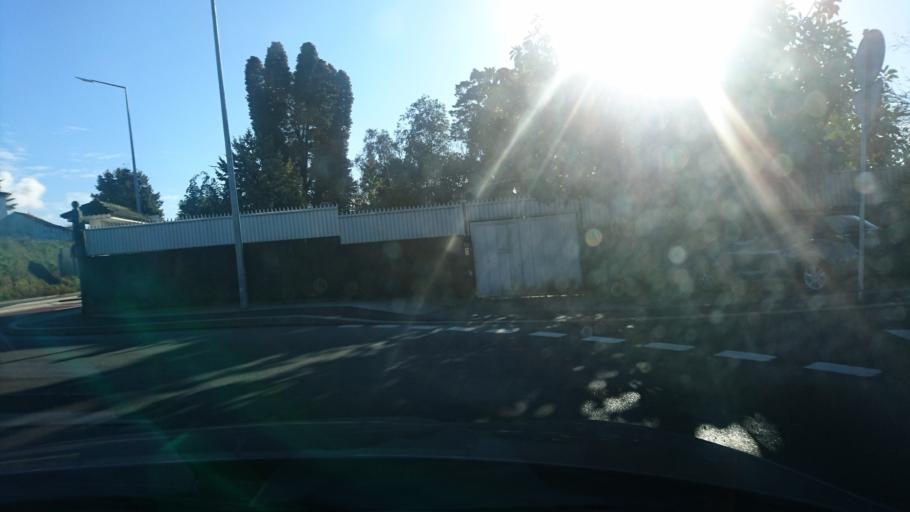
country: PT
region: Aveiro
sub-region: Santa Maria da Feira
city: Feira
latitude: 40.9299
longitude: -8.5503
